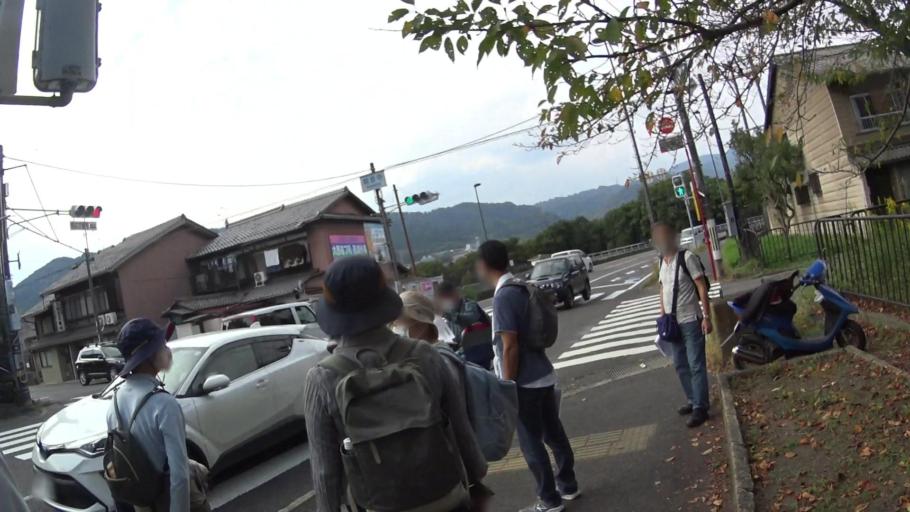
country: JP
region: Osaka
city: Kishiwada
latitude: 34.5022
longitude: 135.3348
